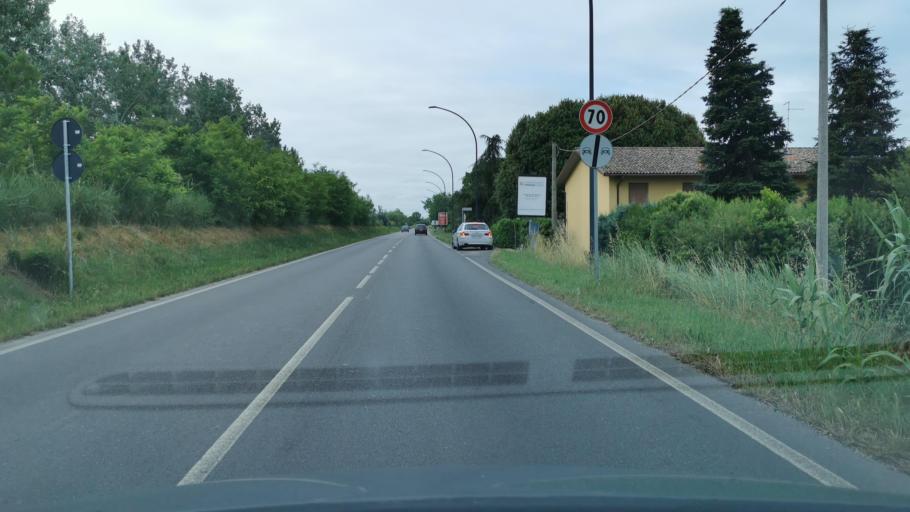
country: IT
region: Emilia-Romagna
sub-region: Provincia di Ravenna
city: Madonna Dell'Albero
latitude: 44.3939
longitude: 12.1972
